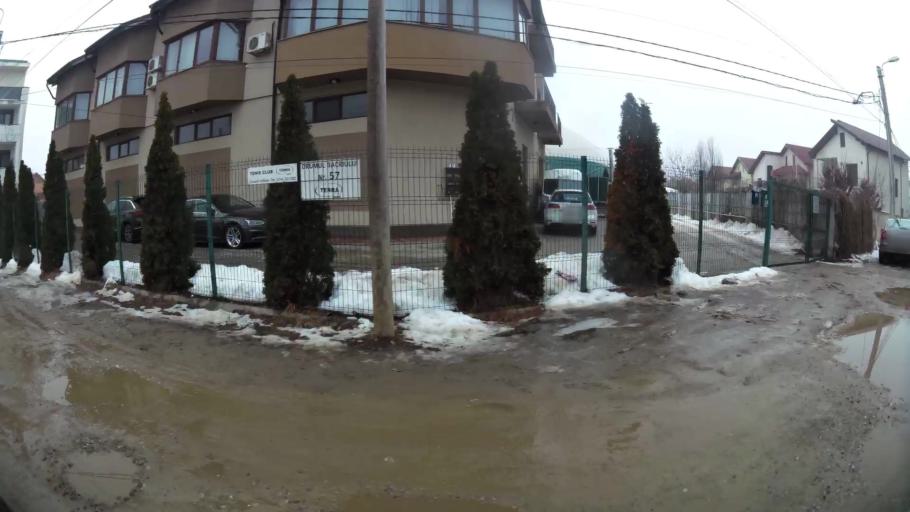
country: RO
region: Ilfov
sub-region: Comuna Chiajna
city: Rosu
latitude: 44.4372
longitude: 25.9989
